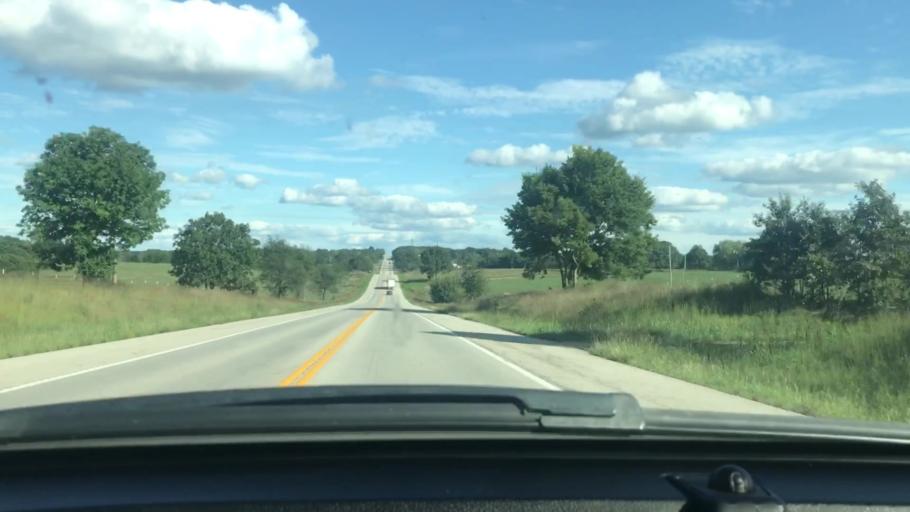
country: US
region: Missouri
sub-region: Howell County
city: West Plains
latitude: 36.6587
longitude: -91.7047
